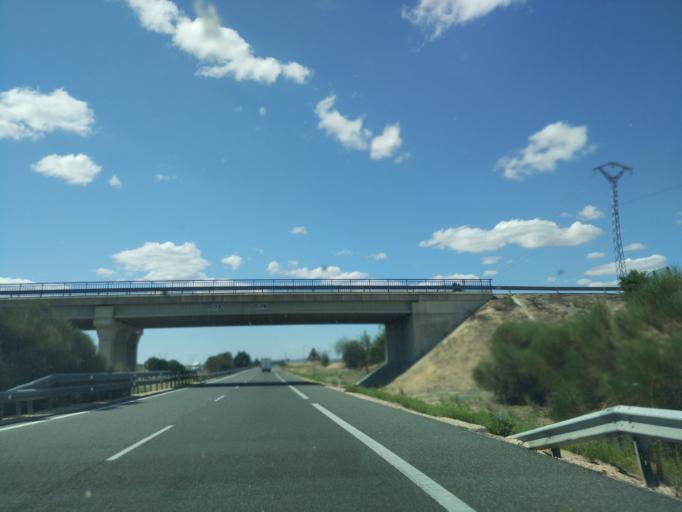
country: ES
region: Castille and Leon
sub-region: Provincia de Valladolid
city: San Vicente del Palacio
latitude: 41.2215
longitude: -4.8435
